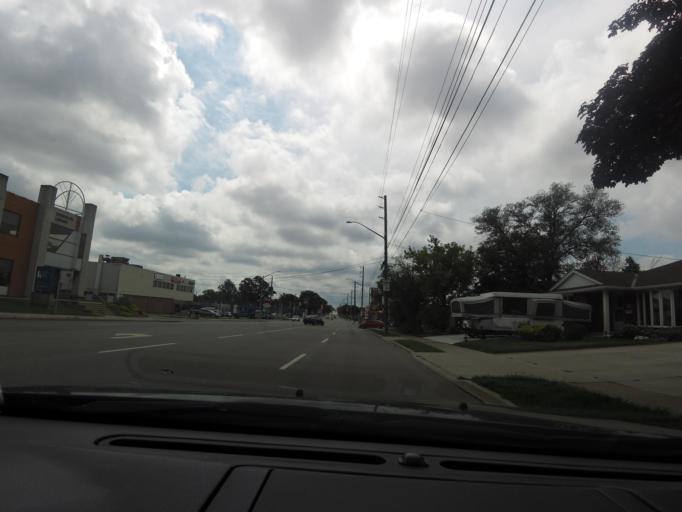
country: CA
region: Ontario
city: Hamilton
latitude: 43.2269
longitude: -79.8290
